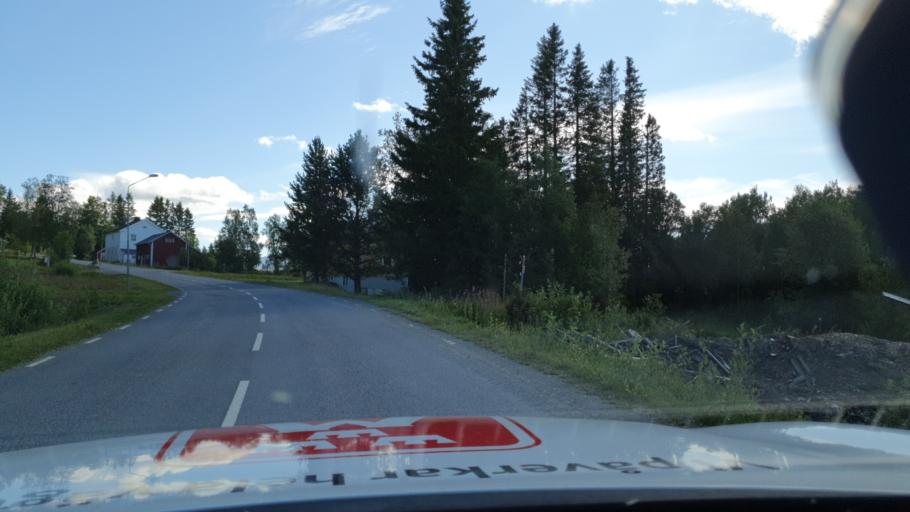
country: SE
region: Jaemtland
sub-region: Are Kommun
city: Are
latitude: 63.5611
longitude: 13.0252
